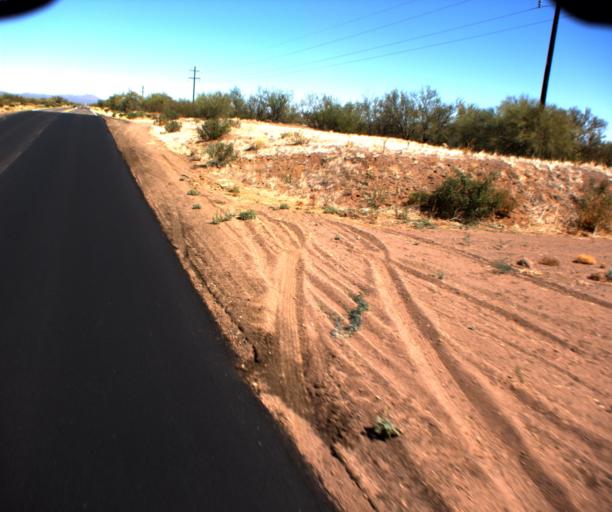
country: US
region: Arizona
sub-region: Pima County
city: Sells
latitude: 32.0240
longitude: -112.0045
